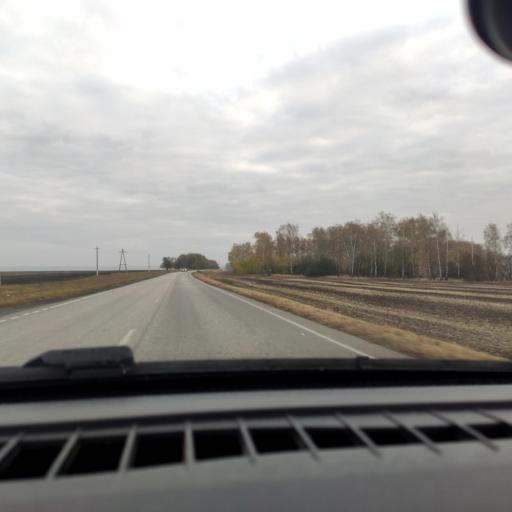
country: RU
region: Belgorod
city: Ilovka
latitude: 50.7553
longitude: 38.7241
